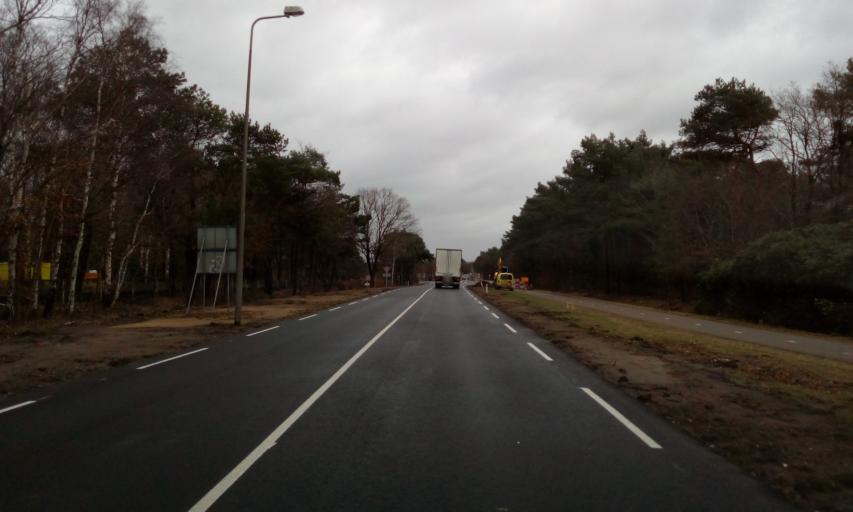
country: NL
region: North Holland
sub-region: Gemeente Bussum
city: Bussum
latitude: 52.2598
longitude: 5.1492
